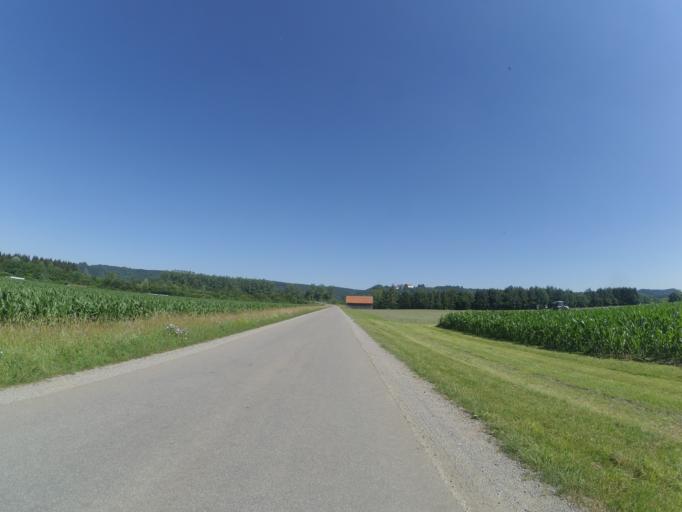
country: DE
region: Baden-Wuerttemberg
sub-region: Tuebingen Region
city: Leutkirch im Allgau
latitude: 47.8496
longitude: 9.9967
